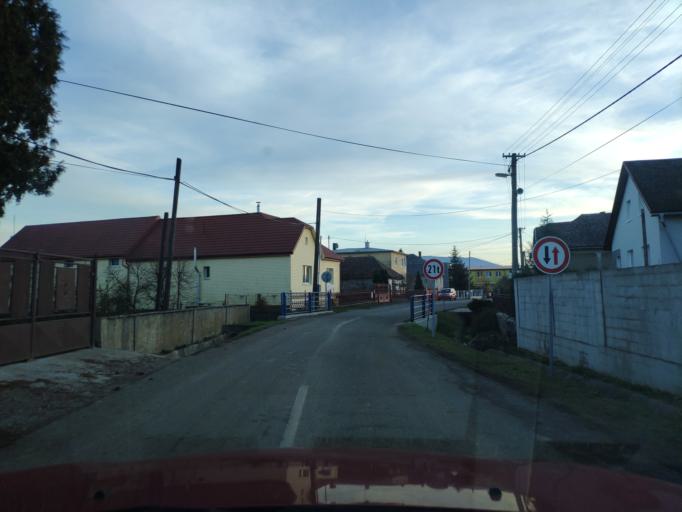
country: SK
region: Kosicky
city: Kosice
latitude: 48.7040
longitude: 21.4126
